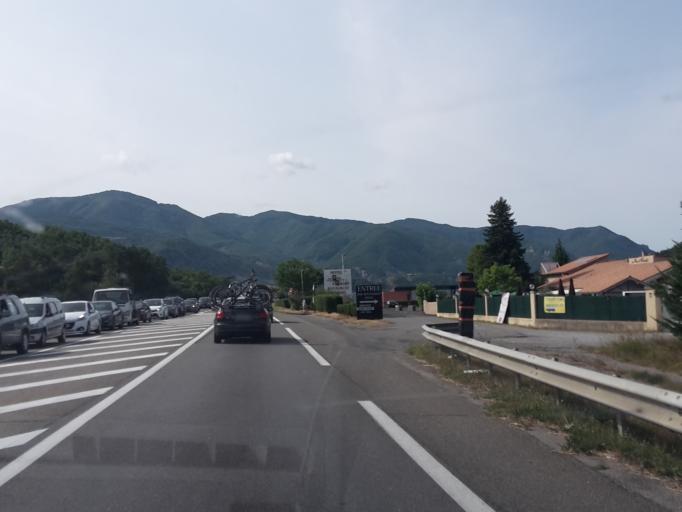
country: FR
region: Provence-Alpes-Cote d'Azur
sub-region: Departement des Hautes-Alpes
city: Tallard
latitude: 44.4472
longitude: 6.0321
